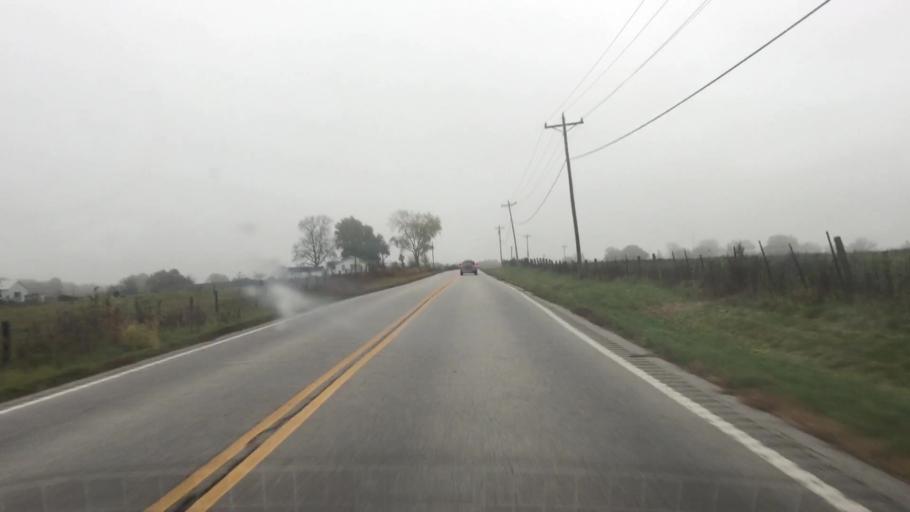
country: US
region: Missouri
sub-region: Callaway County
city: Fulton
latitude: 38.8636
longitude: -92.0100
